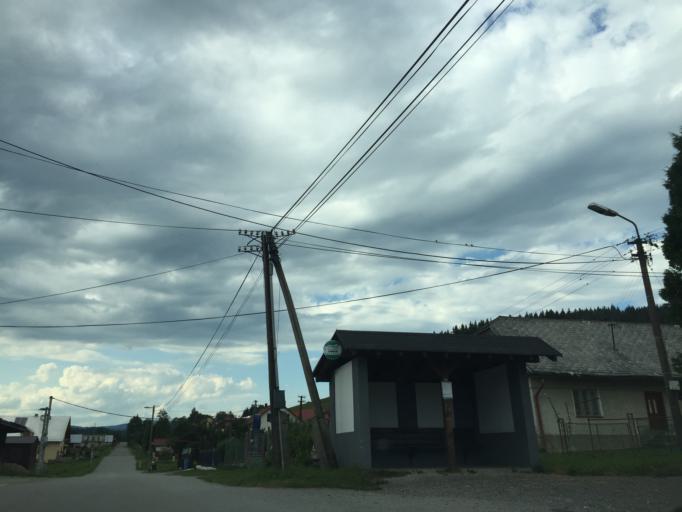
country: PL
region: Silesian Voivodeship
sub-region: Powiat zywiecki
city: Sopotnia Wielka
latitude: 49.4385
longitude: 19.3149
